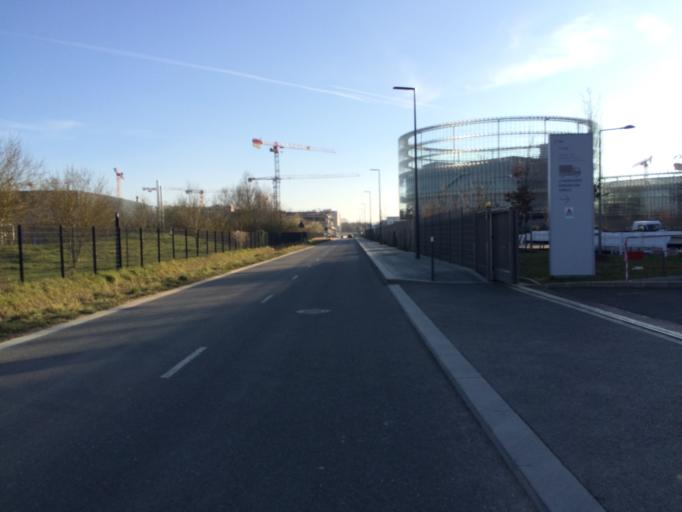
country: FR
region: Ile-de-France
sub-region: Departement de l'Essonne
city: Vauhallan
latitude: 48.7175
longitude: 2.1988
